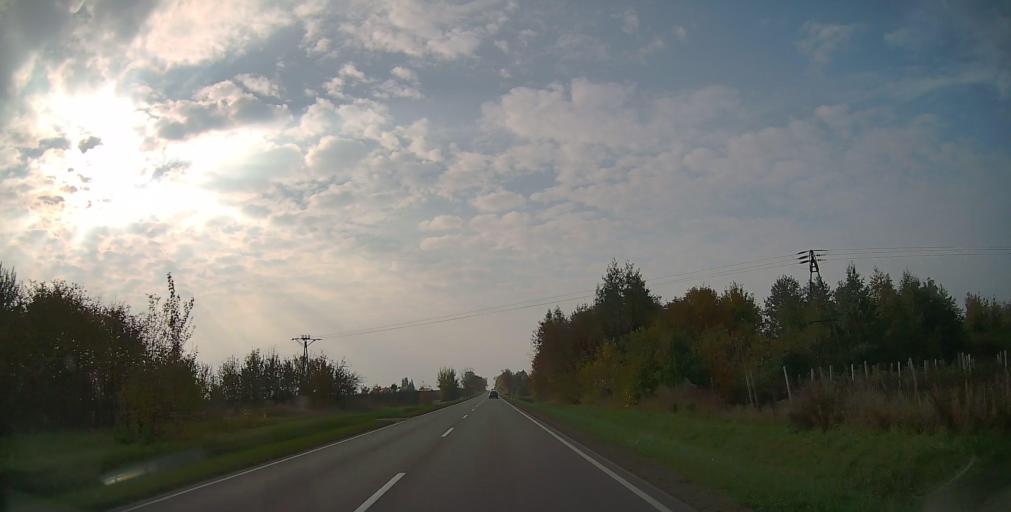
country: PL
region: Masovian Voivodeship
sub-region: Powiat grojecki
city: Bledow
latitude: 51.7597
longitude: 20.7663
